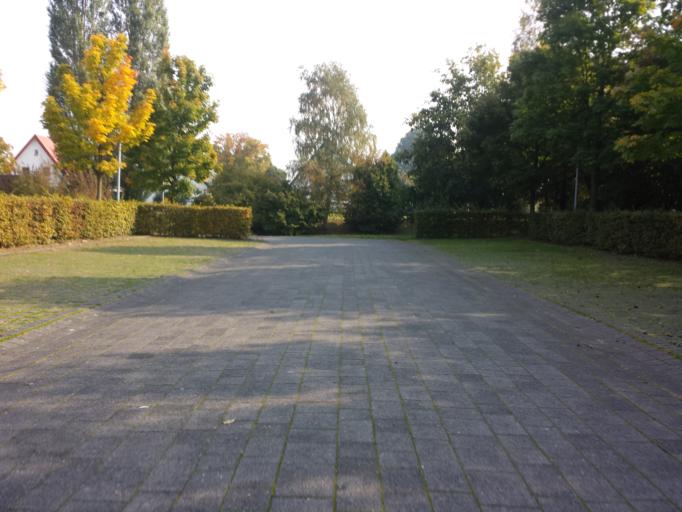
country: DE
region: North Rhine-Westphalia
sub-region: Regierungsbezirk Detmold
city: Guetersloh
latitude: 51.9038
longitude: 8.3503
